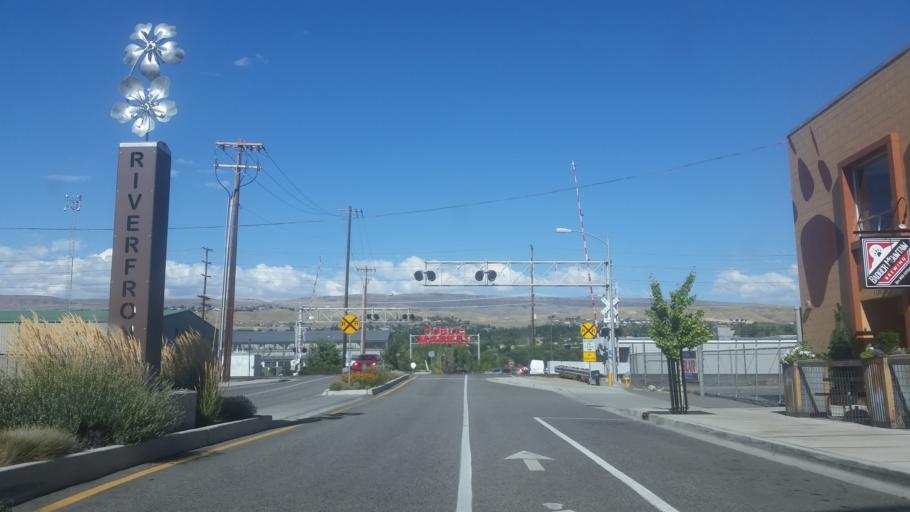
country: US
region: Washington
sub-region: Chelan County
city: Wenatchee
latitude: 47.4240
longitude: -120.3091
